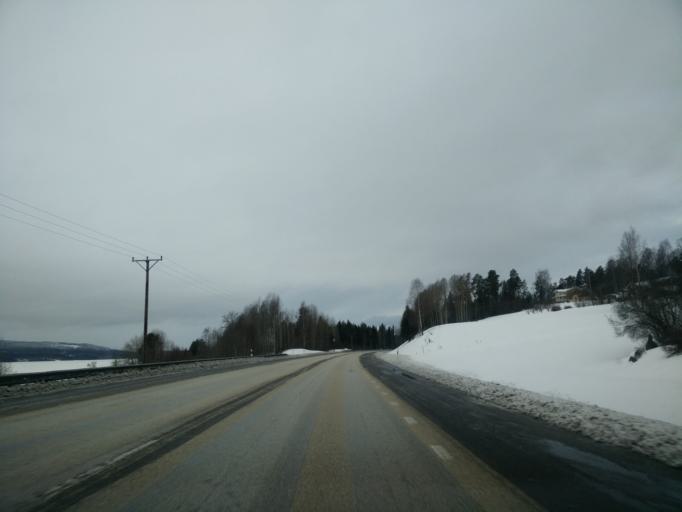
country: SE
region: Vaesternorrland
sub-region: Sundsvalls Kommun
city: Matfors
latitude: 62.3995
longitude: 16.7237
